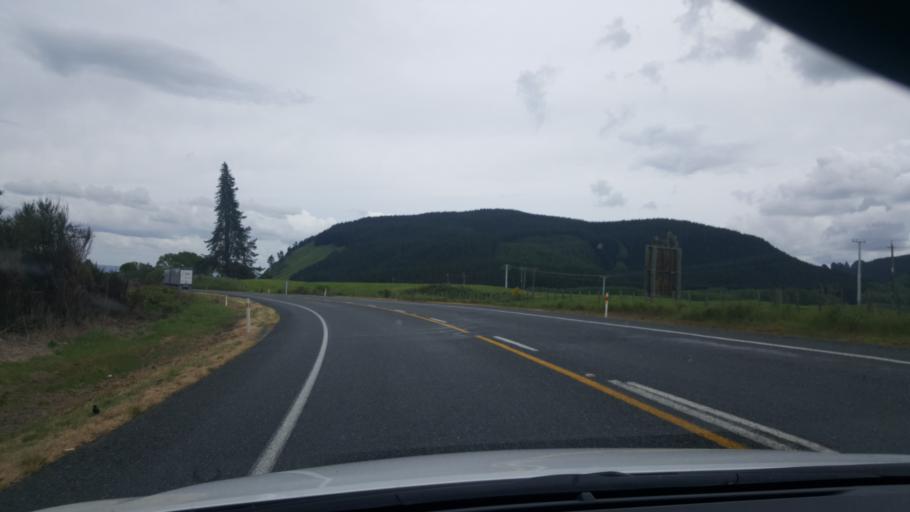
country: NZ
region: Bay of Plenty
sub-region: Rotorua District
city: Rotorua
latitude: -38.3430
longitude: 176.3613
